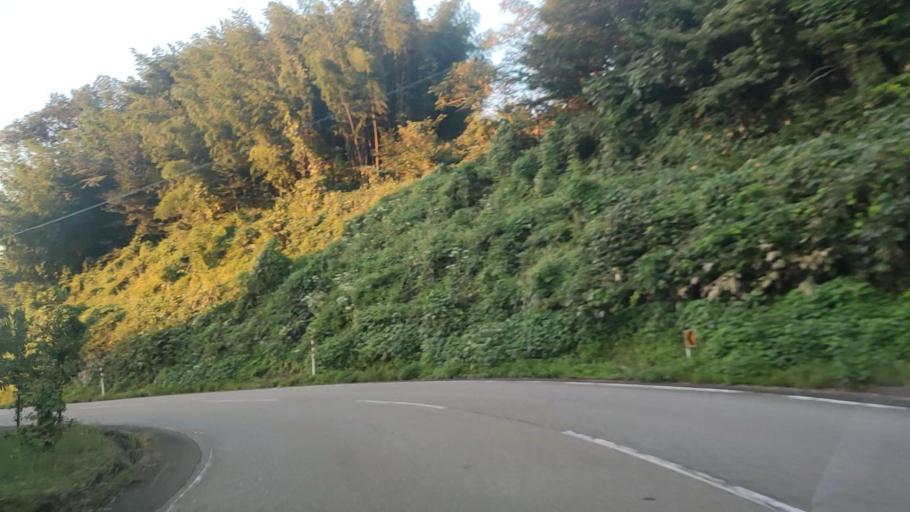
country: JP
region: Ishikawa
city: Tsubata
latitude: 36.6220
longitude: 136.7808
